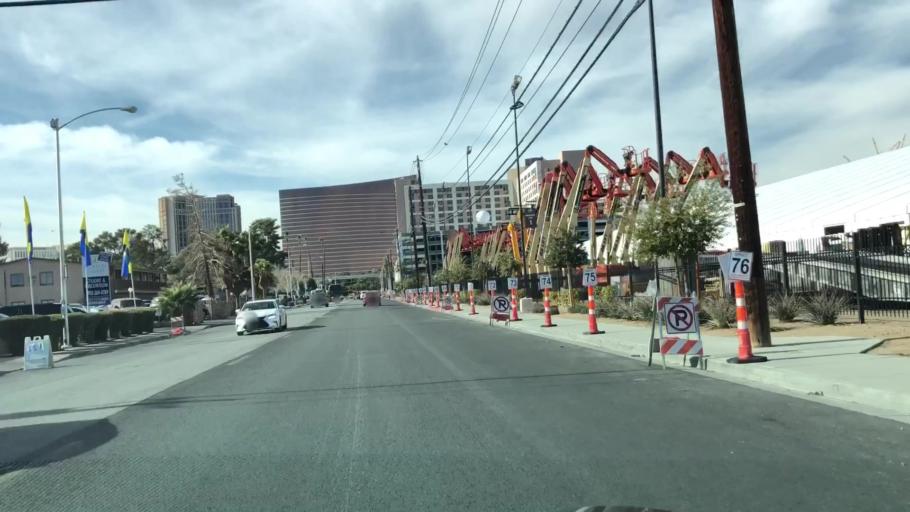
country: US
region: Nevada
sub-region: Clark County
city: Paradise
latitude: 36.1269
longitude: -115.1505
